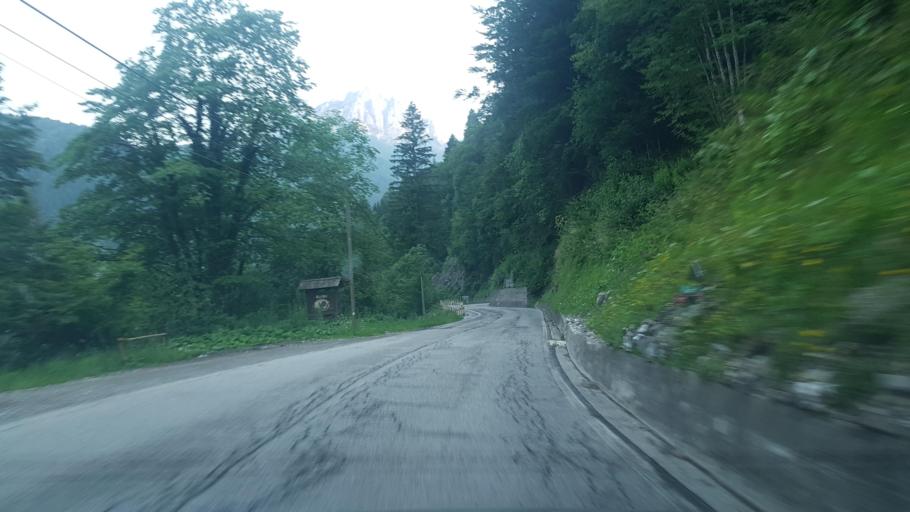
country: IT
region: Friuli Venezia Giulia
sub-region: Provincia di Udine
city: Paularo
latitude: 46.5153
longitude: 13.1227
